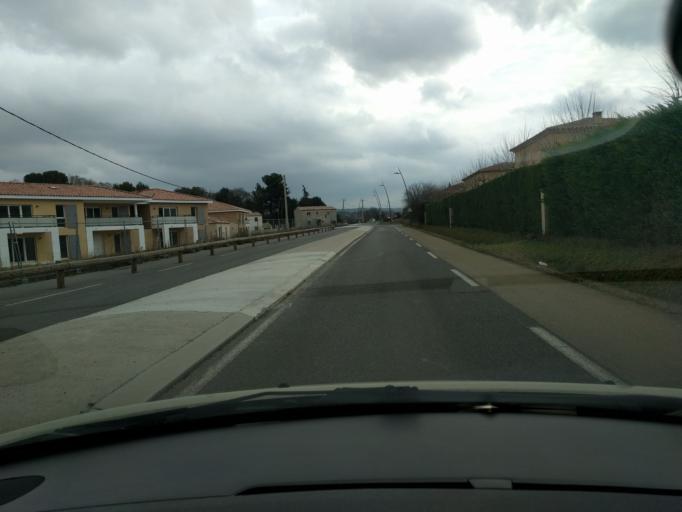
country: FR
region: Provence-Alpes-Cote d'Azur
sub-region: Departement des Bouches-du-Rhone
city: Bouc-Bel-Air
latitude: 43.4344
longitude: 5.4101
